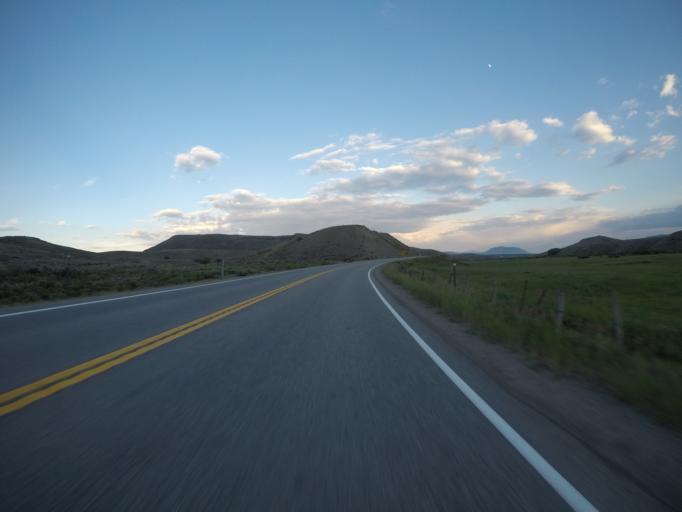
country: US
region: Colorado
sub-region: Grand County
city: Kremmling
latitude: 40.2440
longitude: -106.4437
